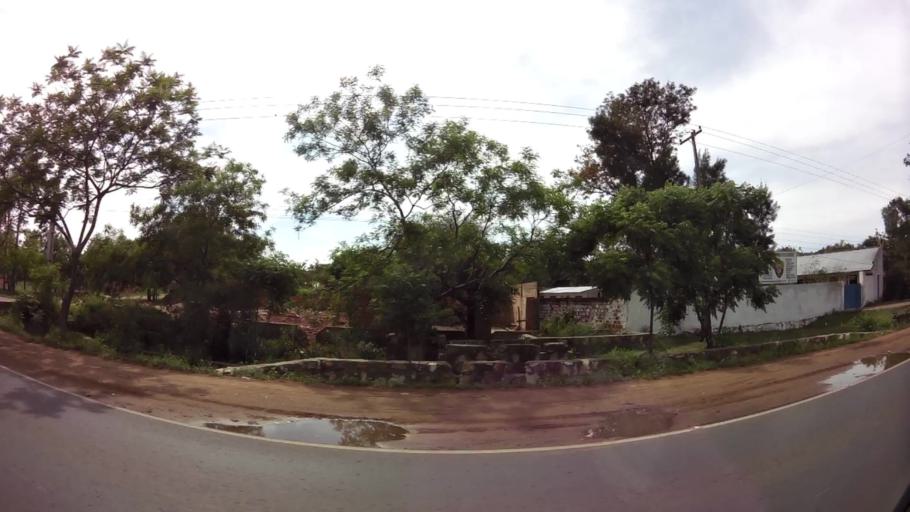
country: PY
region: Central
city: Limpio
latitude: -25.1535
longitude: -57.4732
